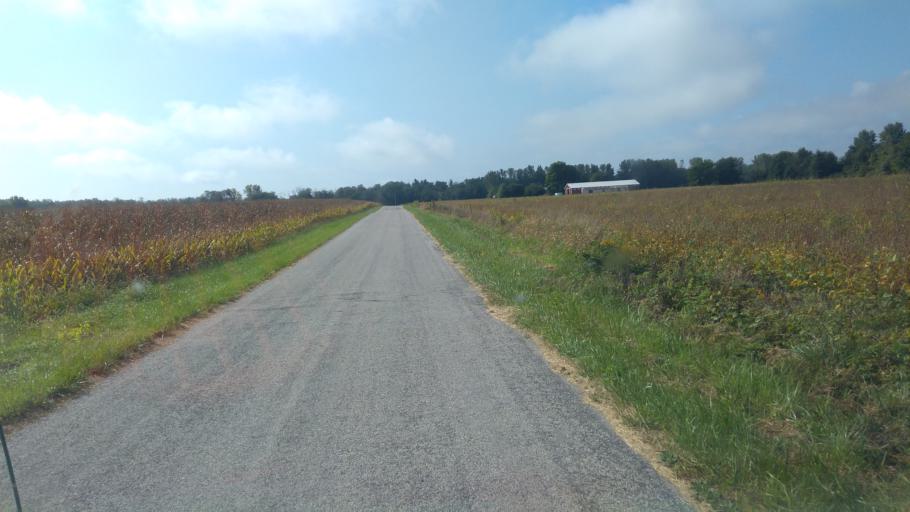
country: US
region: Ohio
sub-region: Morrow County
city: Cardington
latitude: 40.5204
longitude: -82.9340
